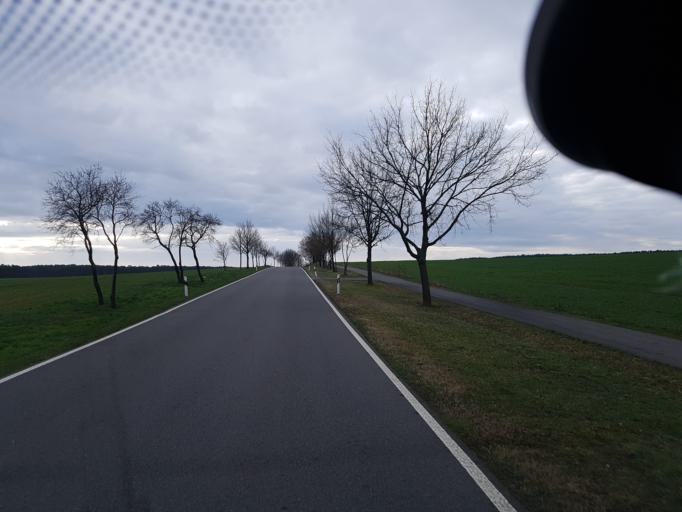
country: DE
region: Brandenburg
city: Gross Lindow
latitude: 52.1562
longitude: 14.5173
